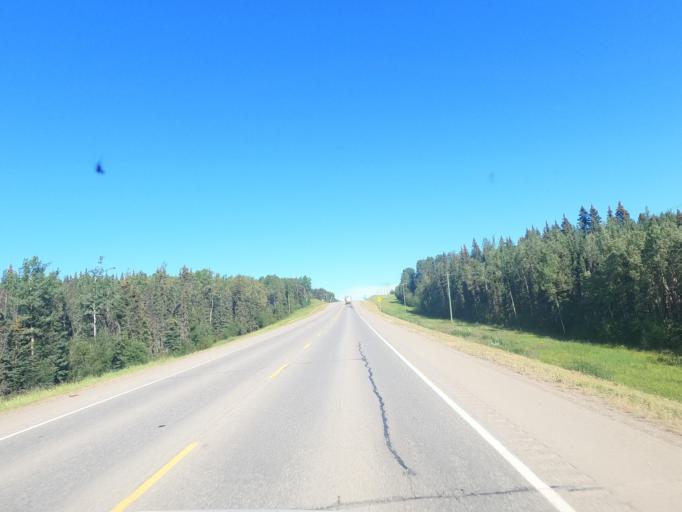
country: CA
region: British Columbia
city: Fort St. John
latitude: 56.6691
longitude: -121.6885
